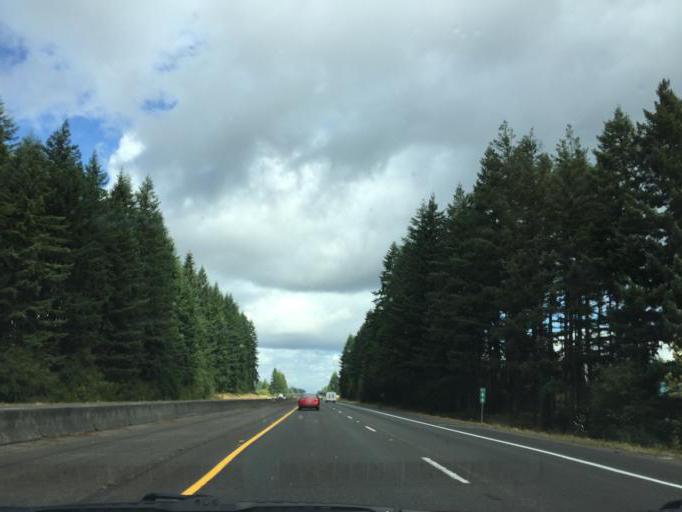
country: US
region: Washington
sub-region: Lewis County
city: Winlock
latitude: 46.5119
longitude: -122.8766
